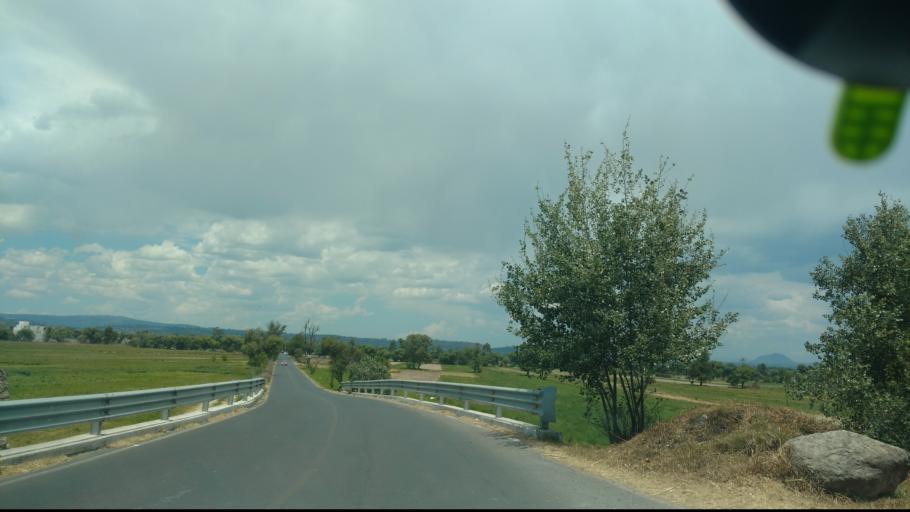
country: MX
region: Puebla
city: San Miguel Xoxtla
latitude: 19.1951
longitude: -98.2865
